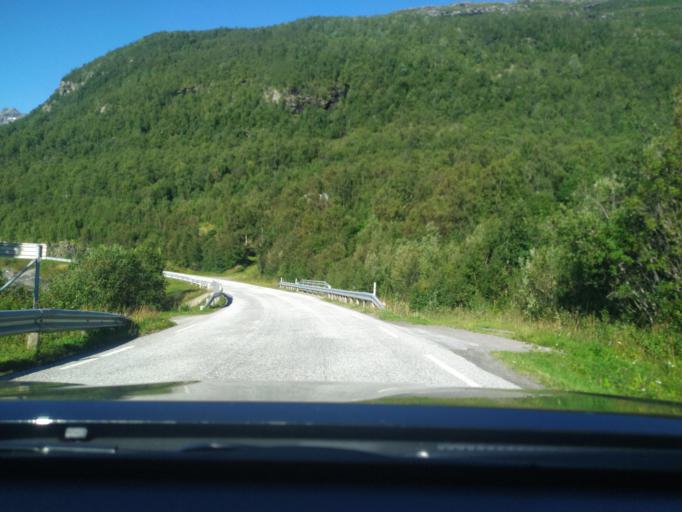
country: NO
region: Troms
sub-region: Dyroy
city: Brostadbotn
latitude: 68.9340
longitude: 17.7005
